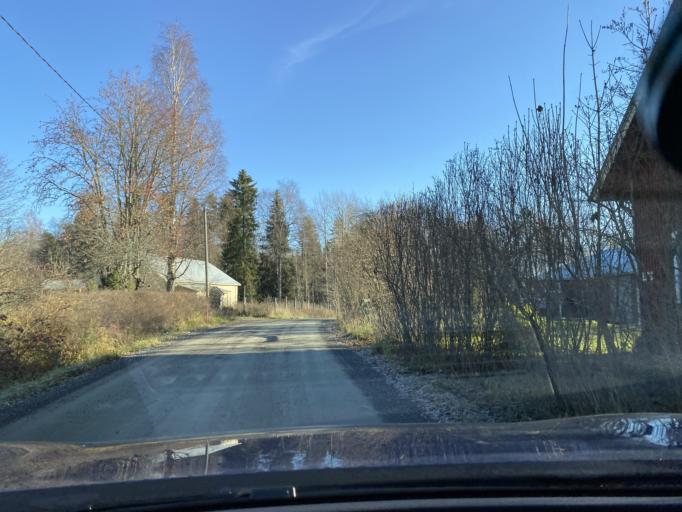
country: FI
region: Haeme
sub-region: Haemeenlinna
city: Kalvola
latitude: 60.9865
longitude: 24.0556
